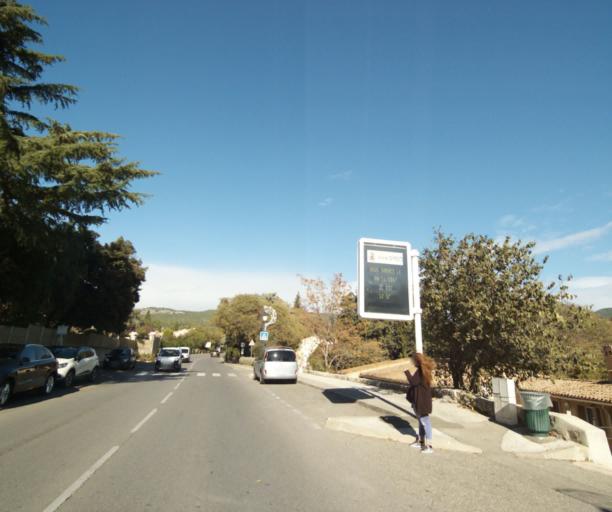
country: FR
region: Provence-Alpes-Cote d'Azur
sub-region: Departement des Bouches-du-Rhone
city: Ceyreste
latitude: 43.2103
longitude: 5.6289
